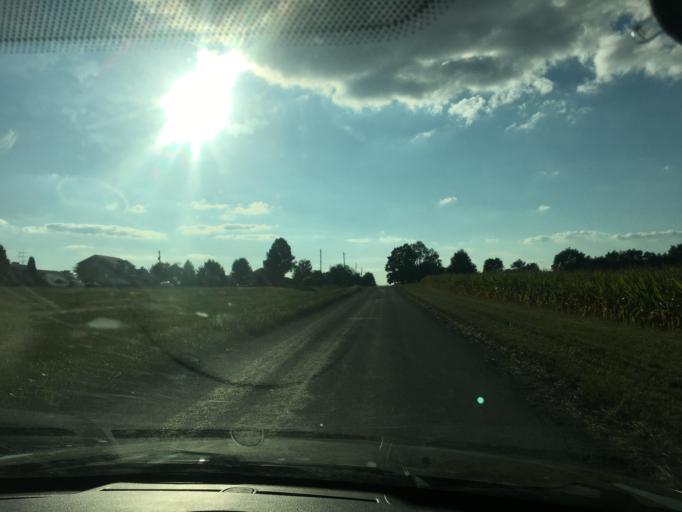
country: US
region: Ohio
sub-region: Logan County
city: West Liberty
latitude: 40.1845
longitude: -83.7494
